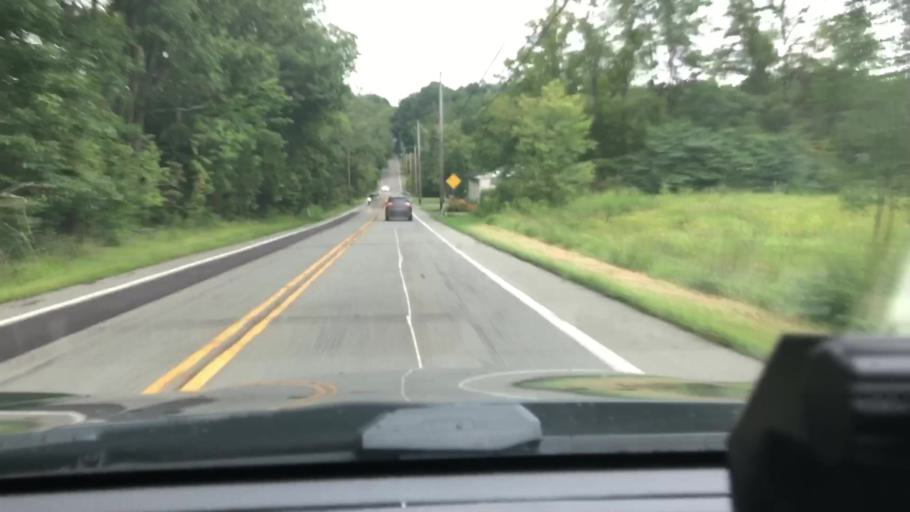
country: US
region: Pennsylvania
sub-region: Montgomery County
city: Gilbertsville
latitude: 40.3407
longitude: -75.5469
